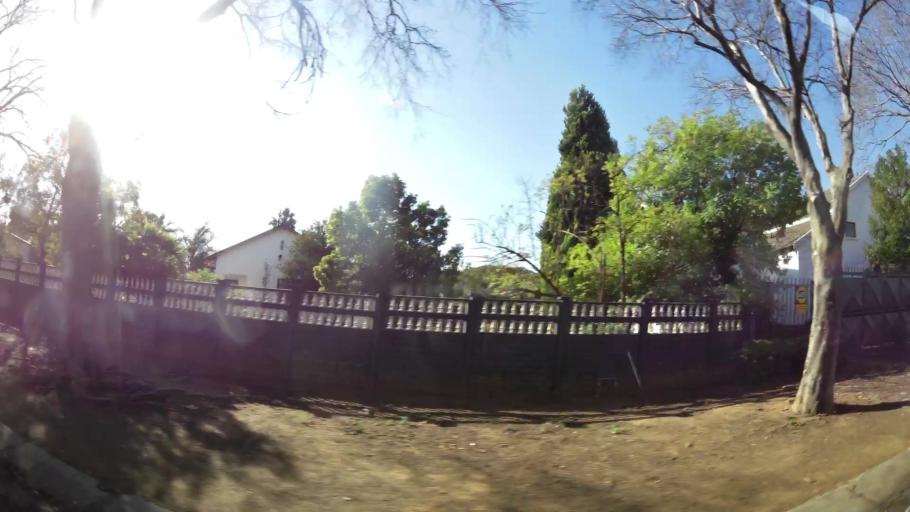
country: ZA
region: Gauteng
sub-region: City of Tshwane Metropolitan Municipality
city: Pretoria
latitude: -25.7081
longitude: 28.2451
